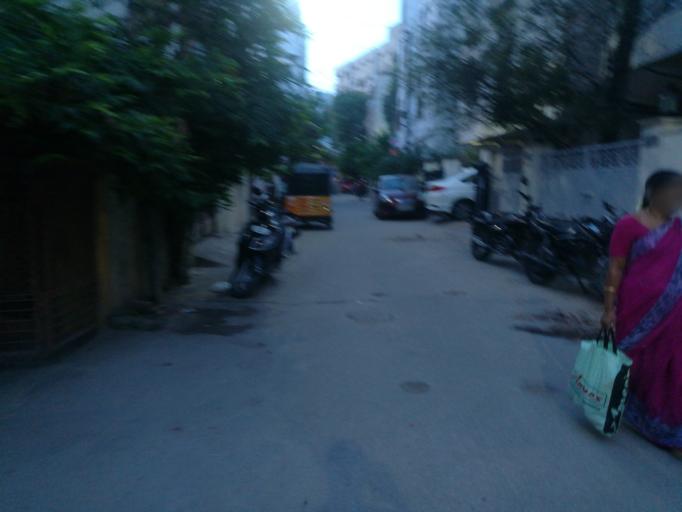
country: IN
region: Telangana
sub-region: Hyderabad
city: Malkajgiri
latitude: 17.4227
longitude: 78.5161
